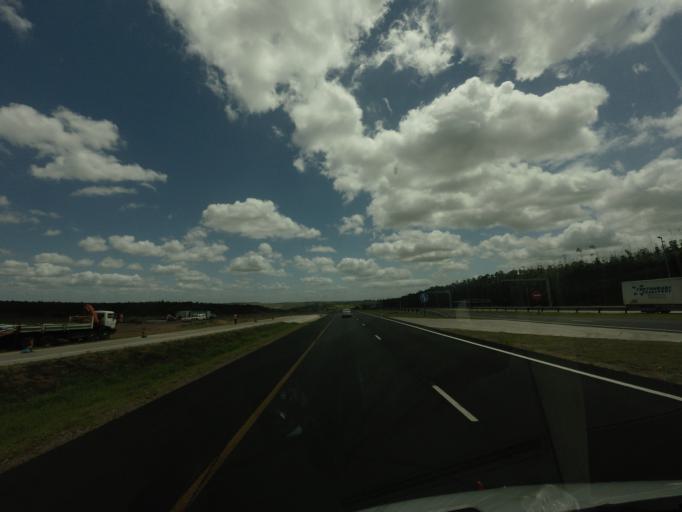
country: ZA
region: KwaZulu-Natal
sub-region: uThungulu District Municipality
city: KwaMbonambi
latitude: -28.5147
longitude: 32.1377
